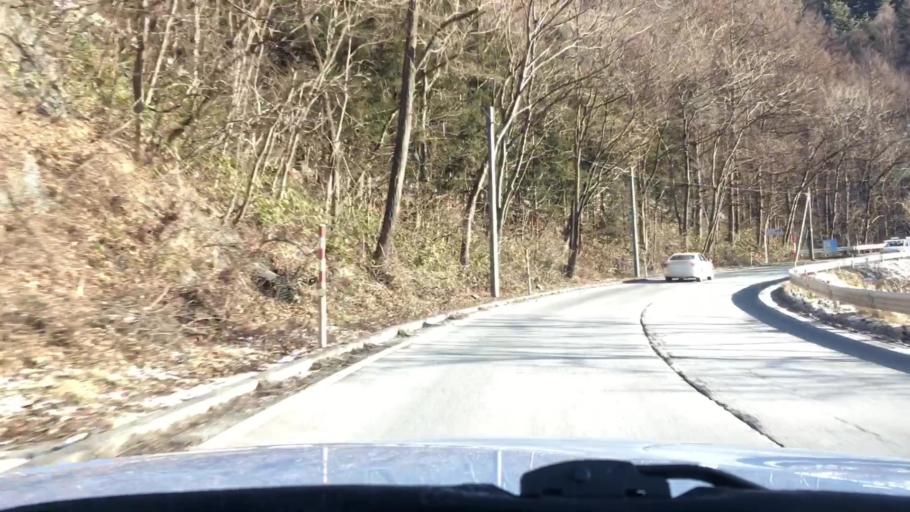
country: JP
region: Iwate
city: Morioka-shi
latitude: 39.6675
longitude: 141.3173
